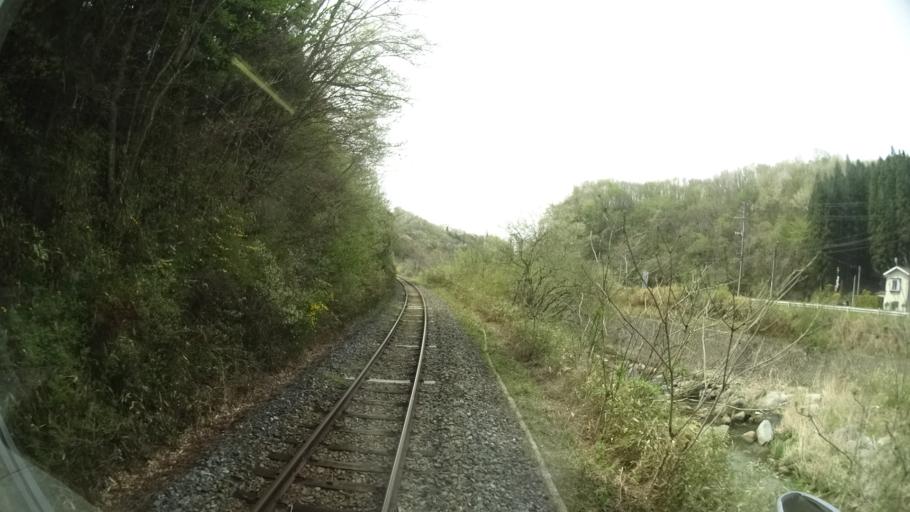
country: JP
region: Iwate
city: Ichinoseki
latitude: 38.9317
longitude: 141.3411
